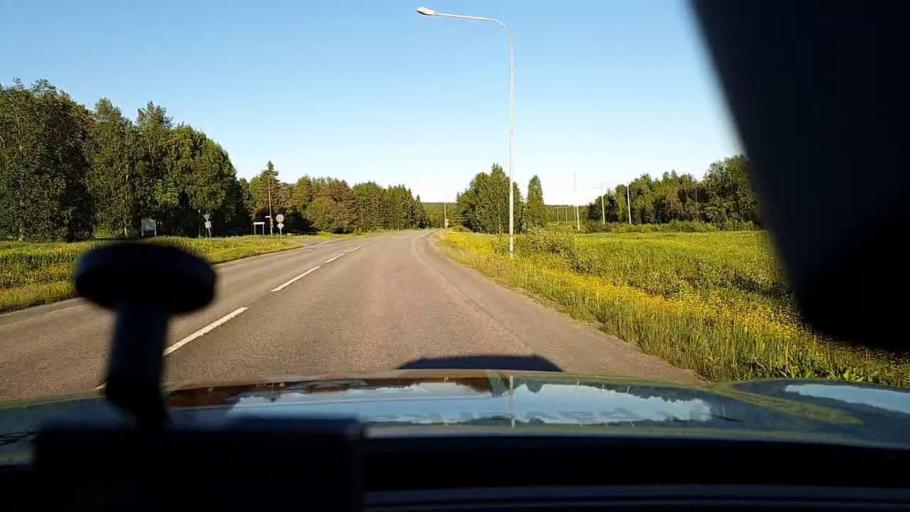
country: SE
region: Norrbotten
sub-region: Lulea Kommun
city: Lulea
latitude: 65.6147
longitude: 22.1514
